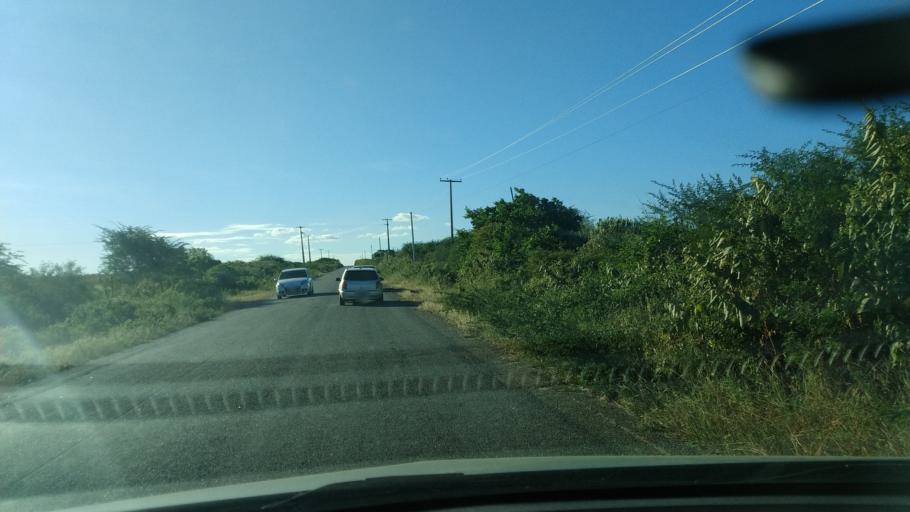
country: BR
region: Rio Grande do Norte
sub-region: Sao Jose Do Campestre
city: Sao Jose do Campestre
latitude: -6.4110
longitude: -35.6519
